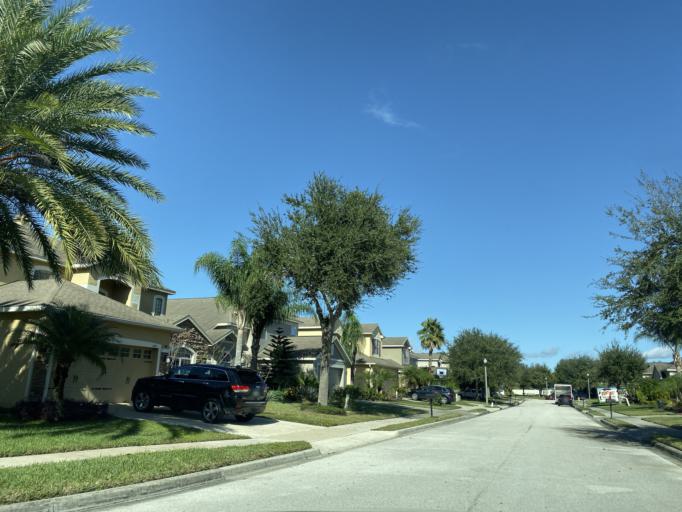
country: US
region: Florida
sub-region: Seminole County
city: Goldenrod
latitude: 28.6134
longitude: -81.2635
